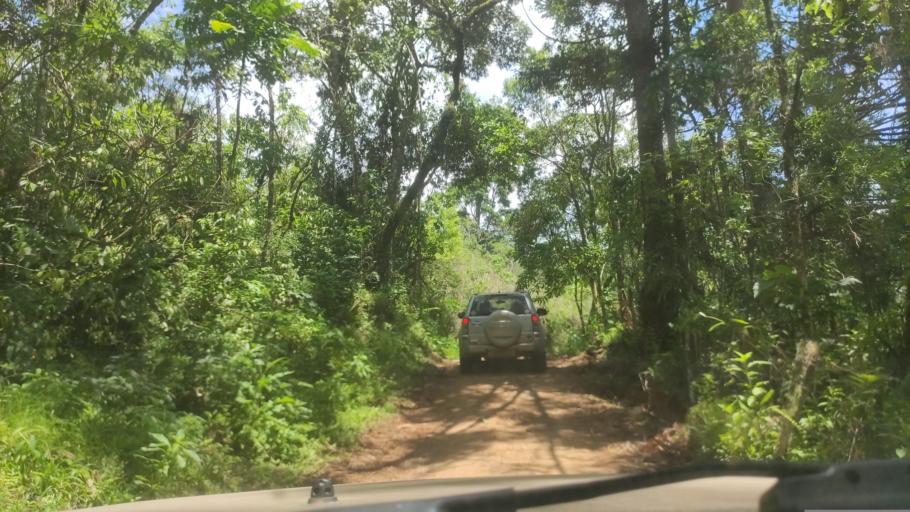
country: BR
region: Minas Gerais
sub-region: Cambui
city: Cambui
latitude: -22.6694
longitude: -45.9457
